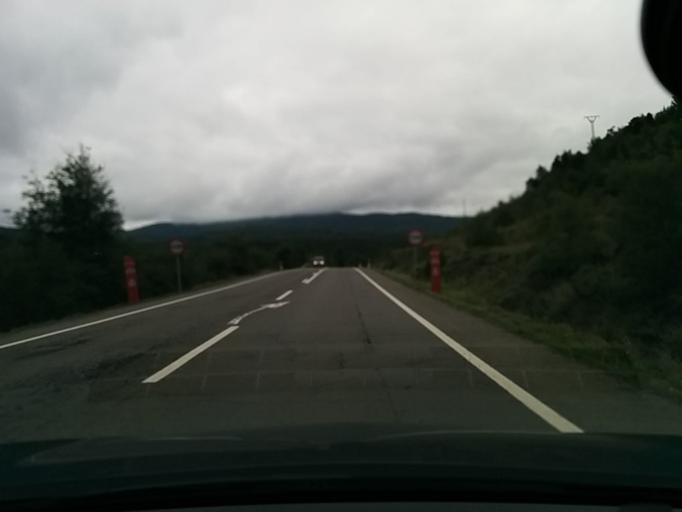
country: ES
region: Aragon
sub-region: Provincia de Huesca
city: Sabinanigo
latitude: 42.4656
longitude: -0.3901
